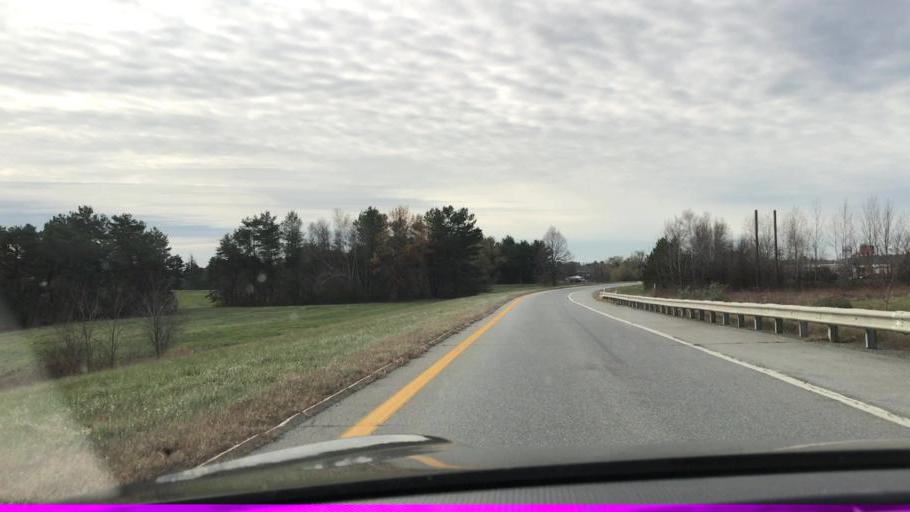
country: US
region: Maine
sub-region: Penobscot County
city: Bangor
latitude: 44.7902
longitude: -68.8072
